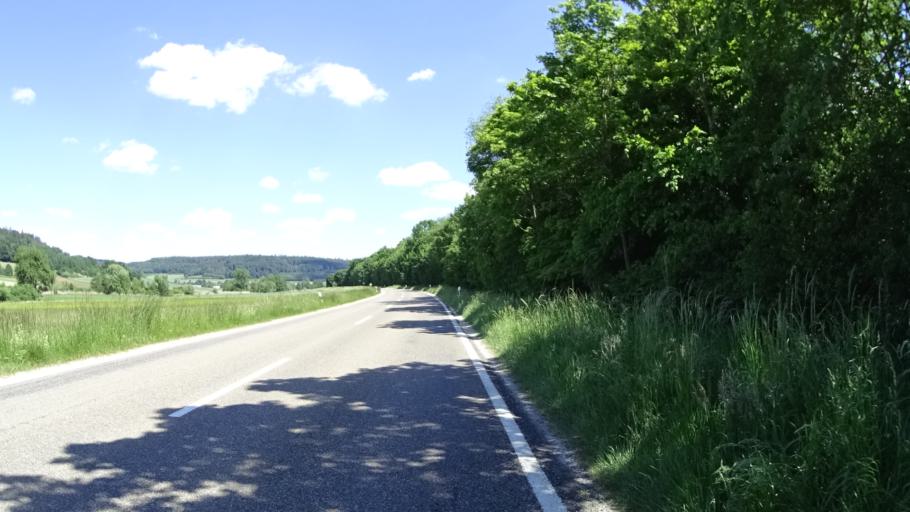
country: DE
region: Bavaria
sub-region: Regierungsbezirk Mittelfranken
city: Thalmassing
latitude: 49.0768
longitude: 11.2710
